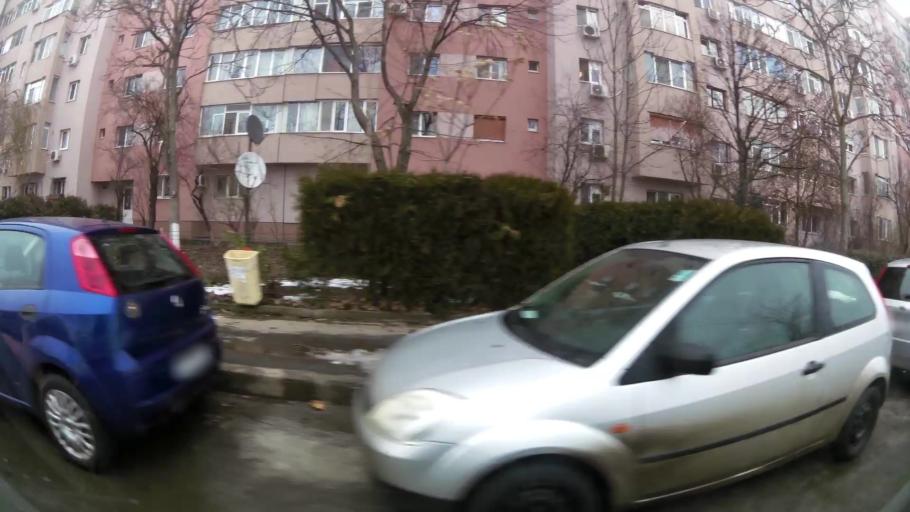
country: RO
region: Ilfov
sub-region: Comuna Chiajna
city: Rosu
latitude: 44.4537
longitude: 26.0394
